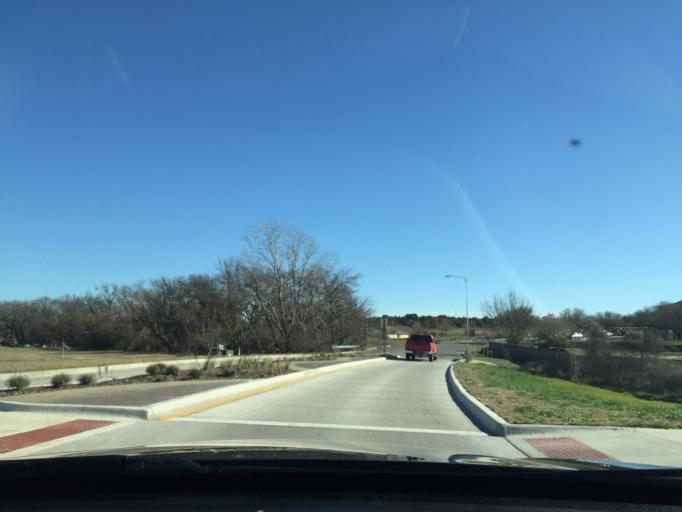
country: US
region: Texas
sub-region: Parker County
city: Weatherford
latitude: 32.7393
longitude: -97.7892
